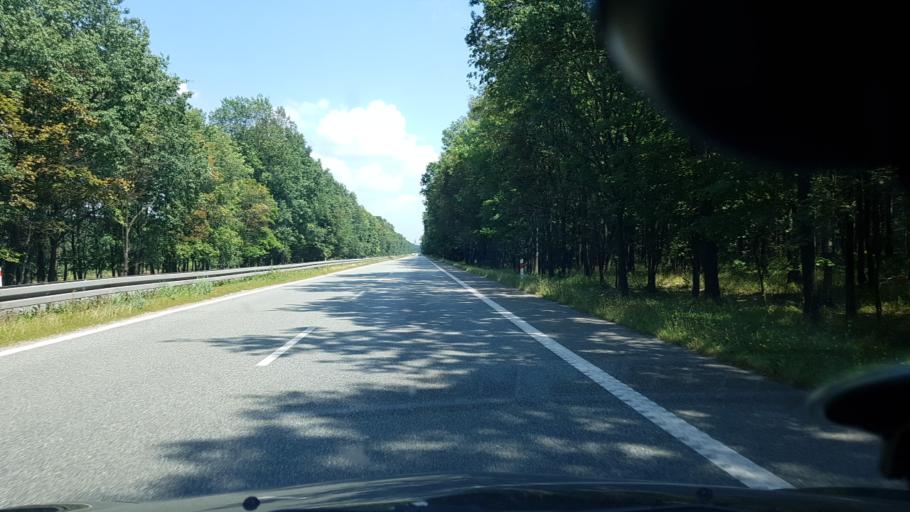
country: PL
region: Silesian Voivodeship
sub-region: Zory
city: Zory
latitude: 50.0665
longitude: 18.7301
